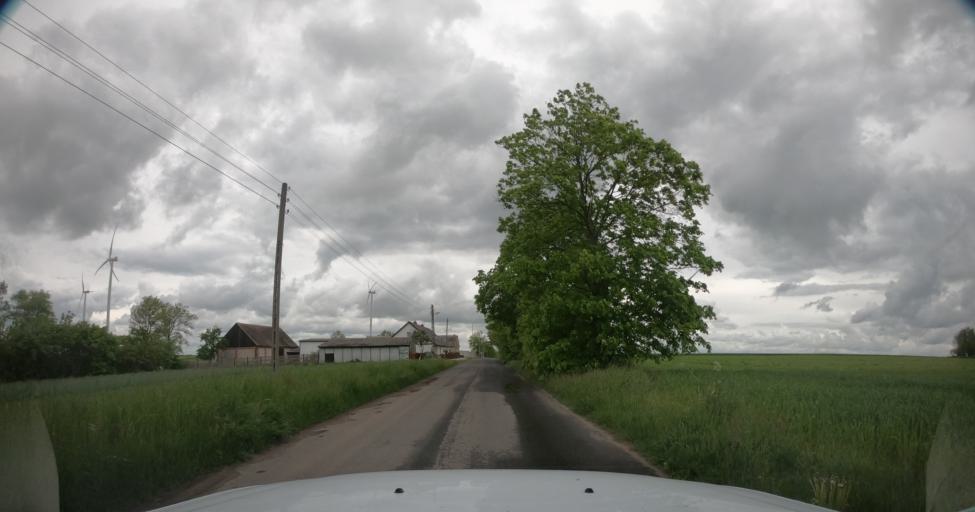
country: PL
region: West Pomeranian Voivodeship
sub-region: Powiat pyrzycki
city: Kozielice
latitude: 53.1110
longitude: 14.8150
